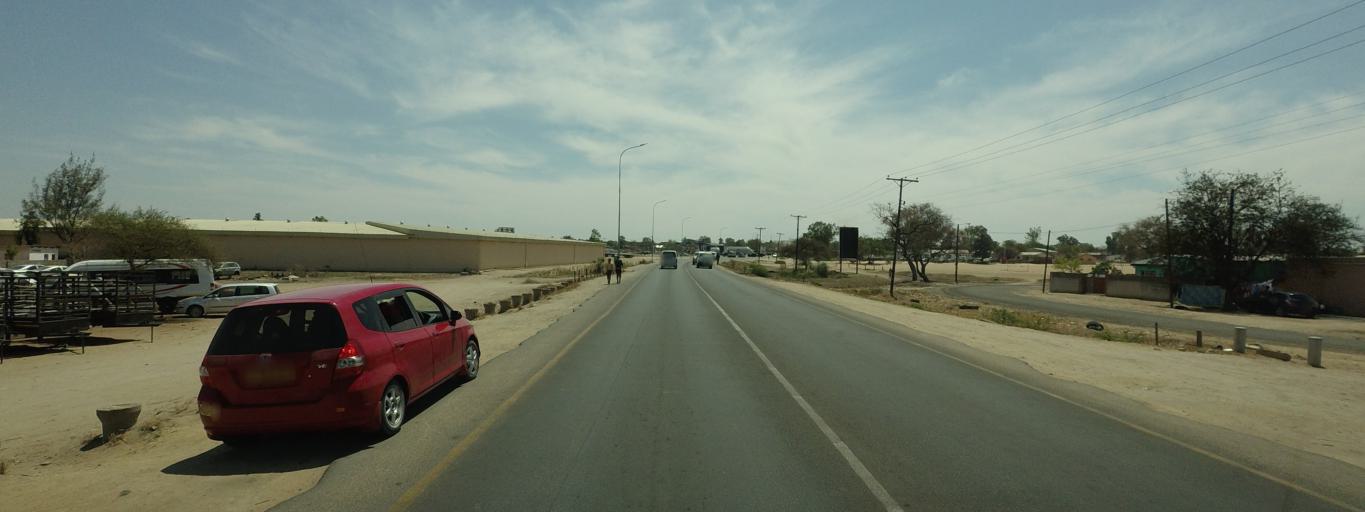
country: BW
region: North East
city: Francistown
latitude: -21.1706
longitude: 27.4987
